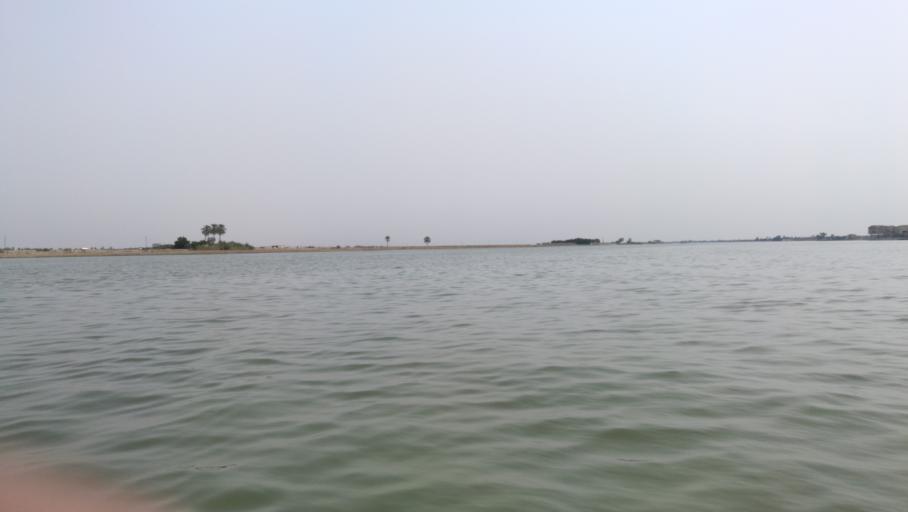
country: IQ
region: Basra Governorate
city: Al Basrah al Qadimah
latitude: 30.5040
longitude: 47.8576
